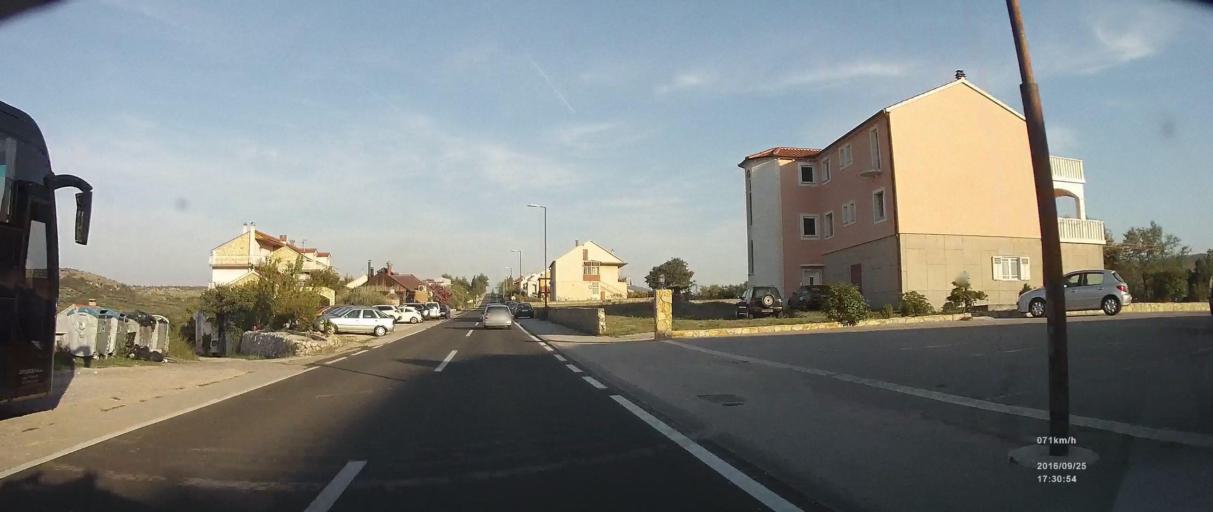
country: HR
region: Sibensko-Kniniska
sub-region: Grad Sibenik
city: Brodarica
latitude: 43.6793
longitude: 15.9831
